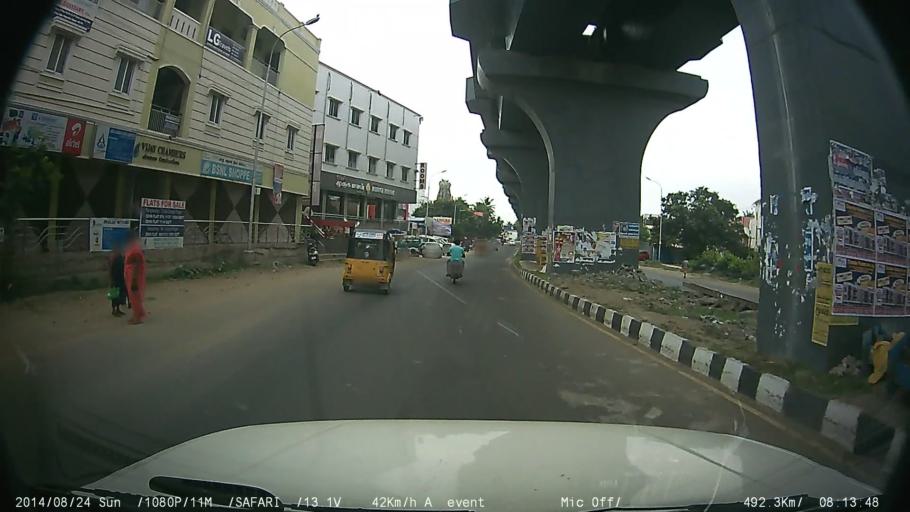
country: IN
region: Tamil Nadu
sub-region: Kancheepuram
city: Saint Thomas Mount
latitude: 12.9875
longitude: 80.1955
